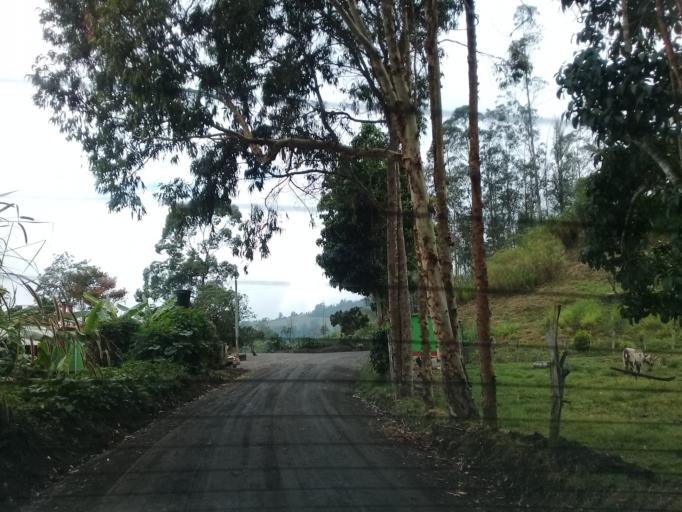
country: CO
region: Cundinamarca
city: Caqueza
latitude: 4.3962
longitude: -73.9822
